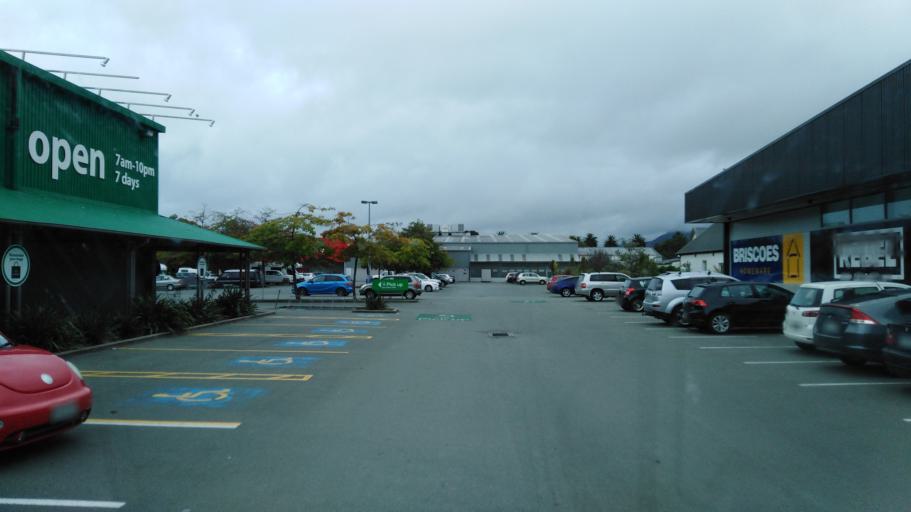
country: NZ
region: Nelson
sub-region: Nelson City
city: Nelson
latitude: -41.2731
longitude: 173.2780
